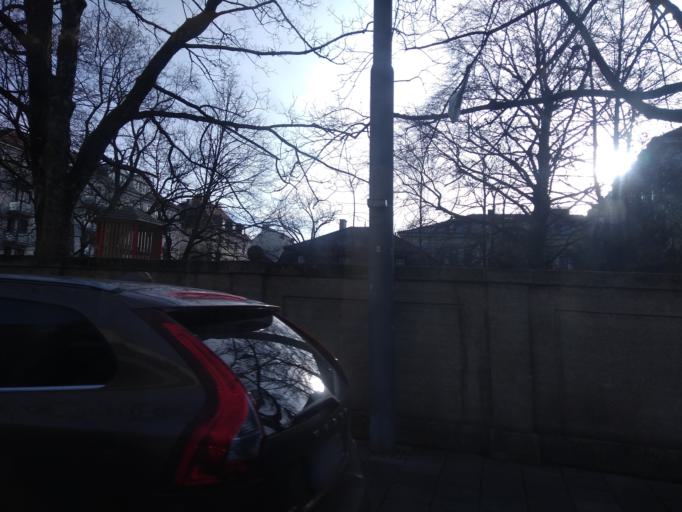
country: DE
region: Bavaria
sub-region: Upper Bavaria
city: Munich
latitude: 48.1624
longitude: 11.5830
